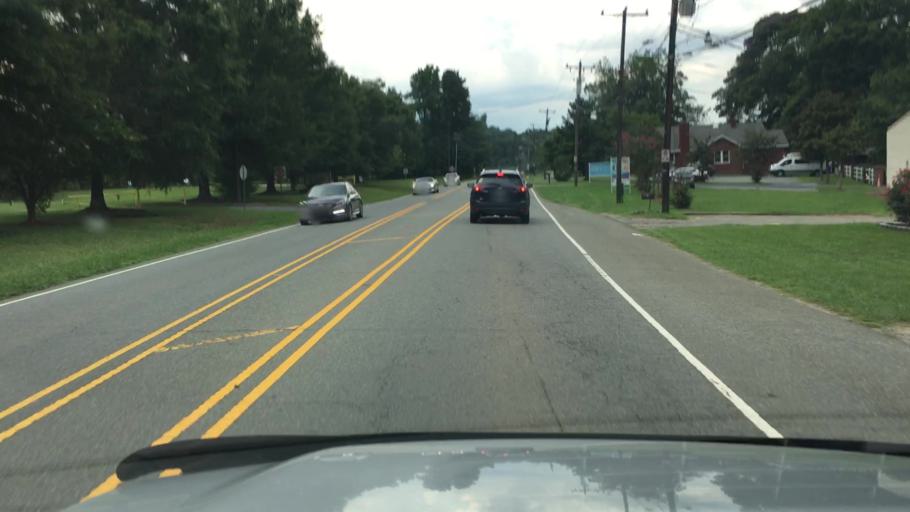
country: US
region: North Carolina
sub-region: Mecklenburg County
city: Huntersville
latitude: 35.3249
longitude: -80.8667
